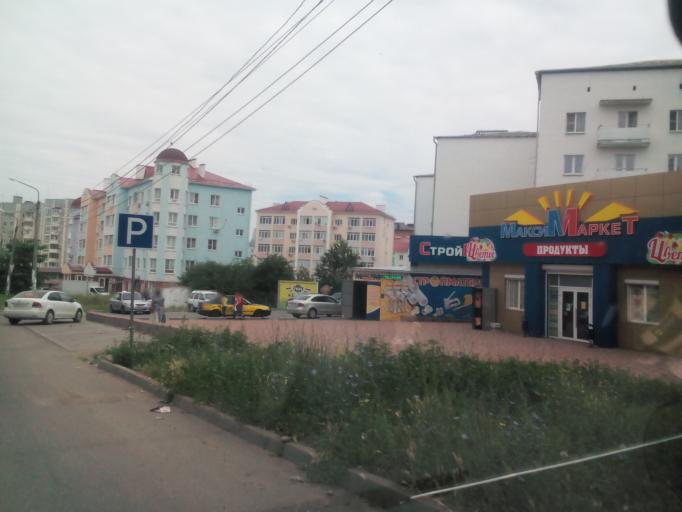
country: RU
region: Stavropol'skiy
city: Zheleznovodsk
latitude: 44.1508
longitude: 43.0021
